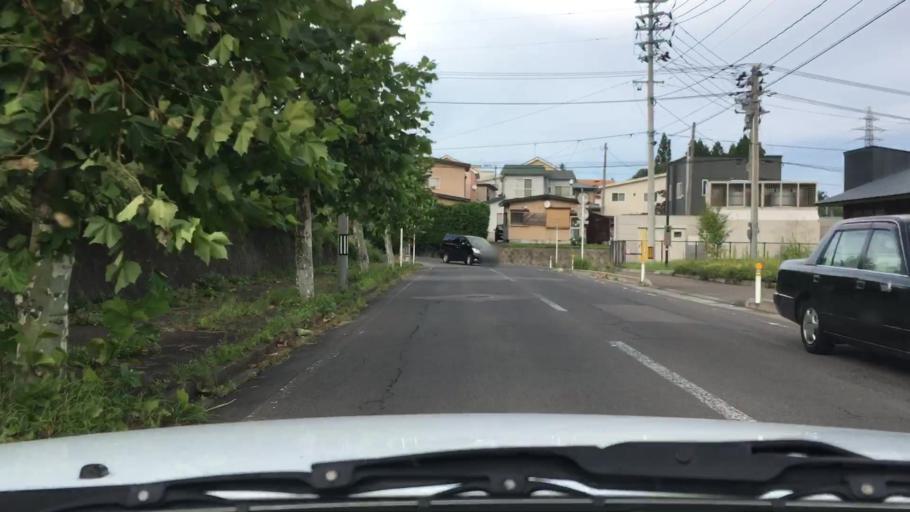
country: JP
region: Aomori
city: Hirosaki
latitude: 40.5775
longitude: 140.4567
